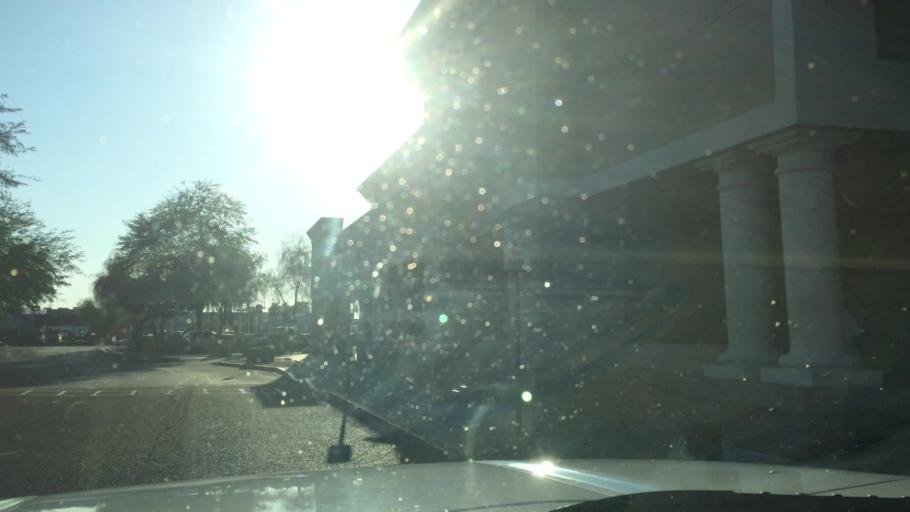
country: US
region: Arizona
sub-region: Maricopa County
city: Sun City
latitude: 33.6394
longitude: -112.2519
